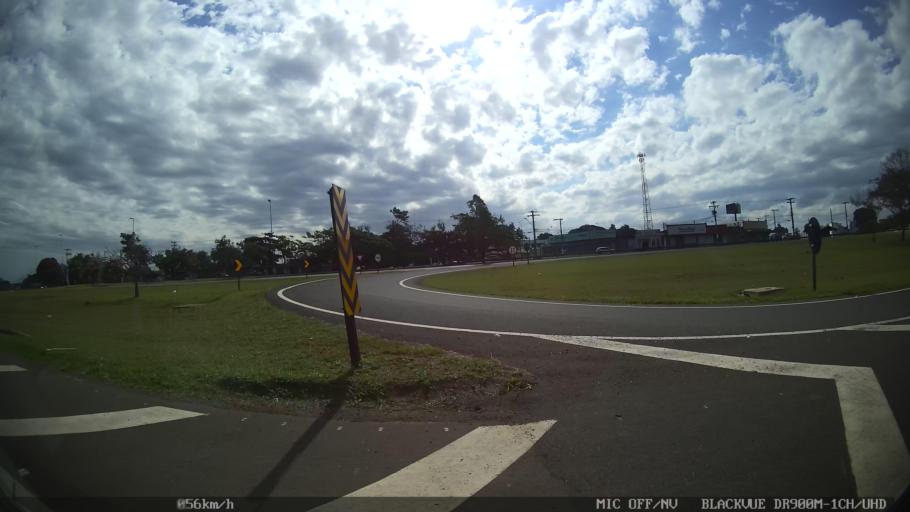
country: BR
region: Sao Paulo
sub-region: Limeira
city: Limeira
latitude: -22.5675
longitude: -47.4394
